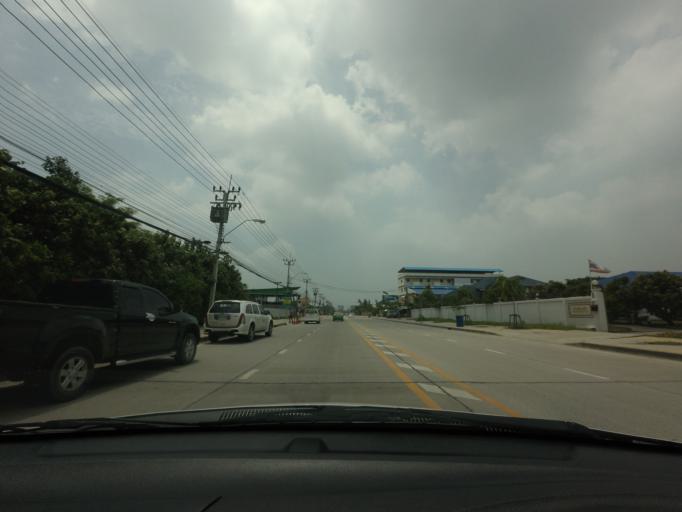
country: TH
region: Bangkok
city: Suan Luang
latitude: 13.6918
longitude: 100.7022
